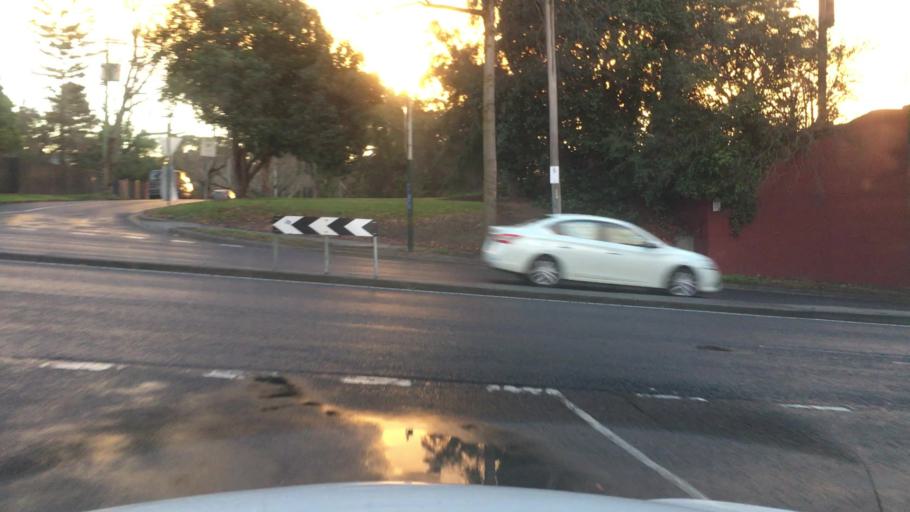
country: AU
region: Victoria
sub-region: Whitehorse
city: Box Hill
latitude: -37.8185
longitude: 145.1149
